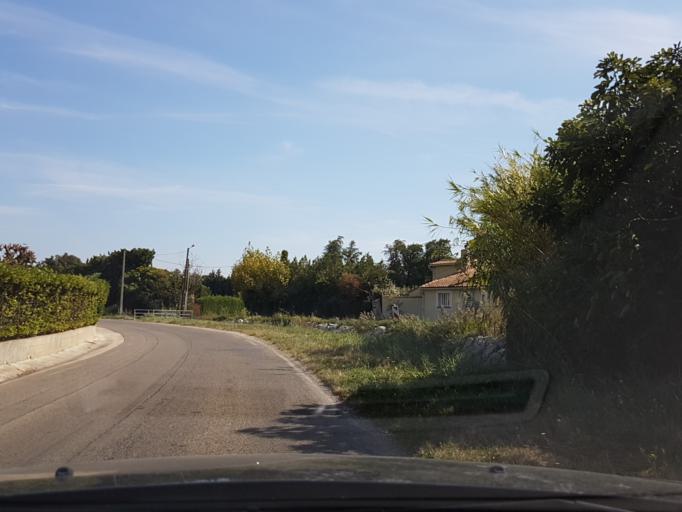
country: FR
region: Provence-Alpes-Cote d'Azur
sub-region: Departement des Bouches-du-Rhone
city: Noves
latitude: 43.8746
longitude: 4.9078
